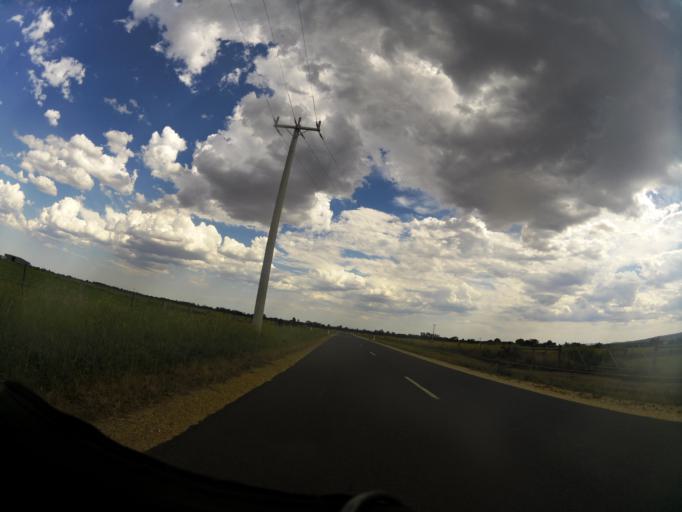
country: AU
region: Victoria
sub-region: Wellington
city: Heyfield
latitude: -37.9948
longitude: 146.6922
